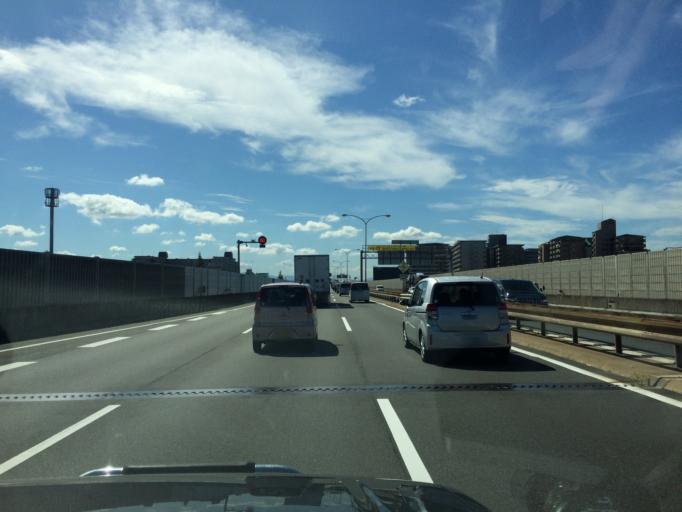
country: JP
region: Osaka
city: Daitocho
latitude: 34.6712
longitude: 135.5980
